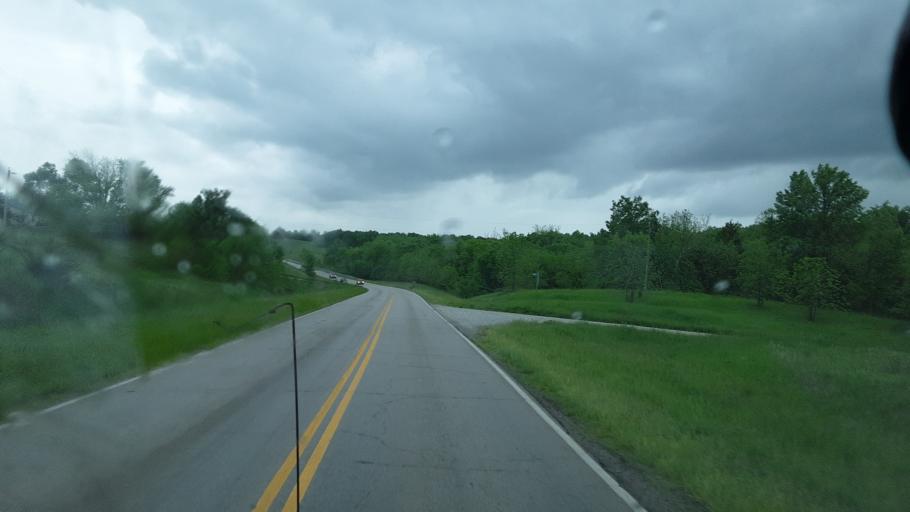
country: US
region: Missouri
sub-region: Monroe County
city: Paris
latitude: 39.4536
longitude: -92.2107
